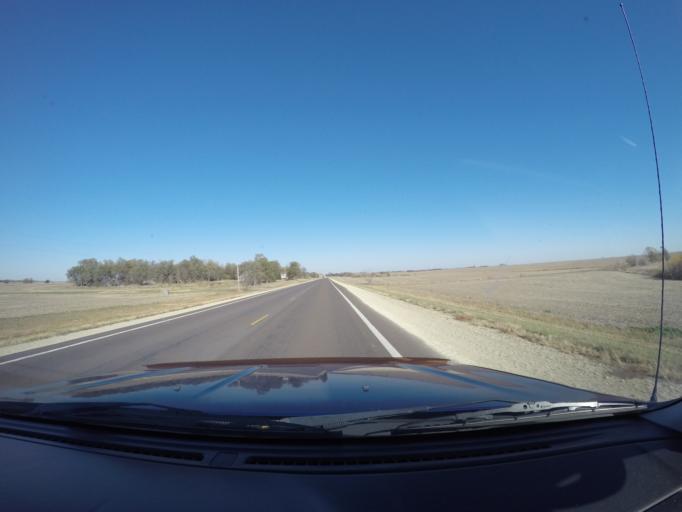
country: US
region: Kansas
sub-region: Marshall County
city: Blue Rapids
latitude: 39.6126
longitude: -96.7504
